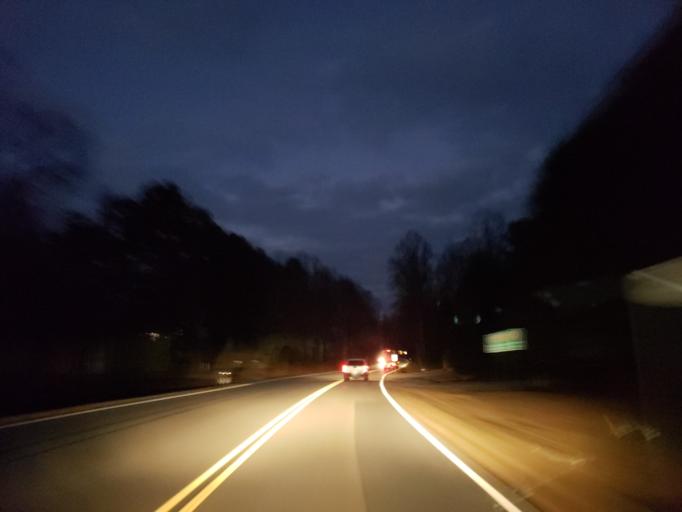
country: US
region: Georgia
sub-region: Polk County
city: Rockmart
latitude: 33.9535
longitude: -84.9995
